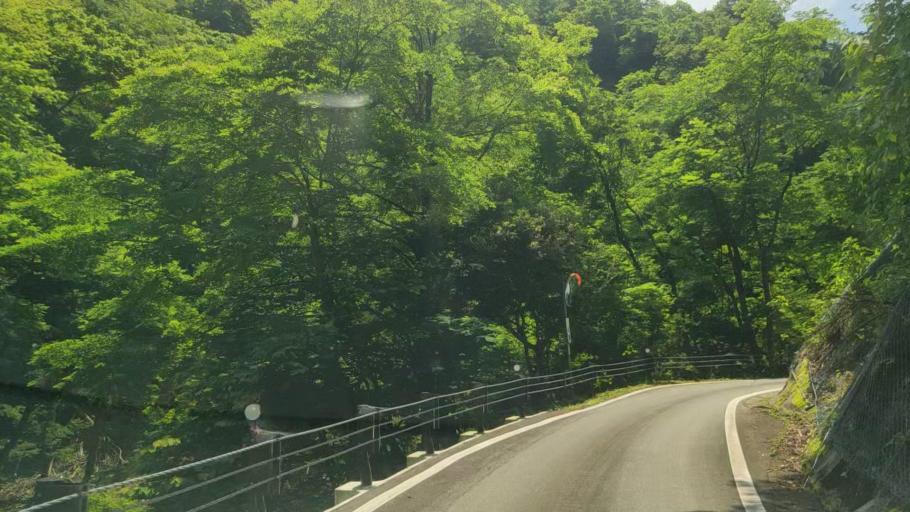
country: JP
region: Tottori
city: Tottori
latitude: 35.4030
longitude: 134.5022
